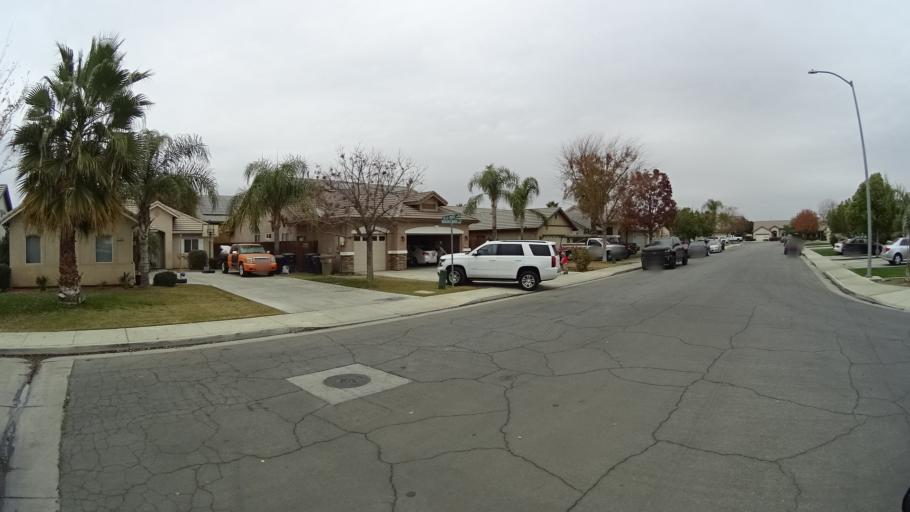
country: US
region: California
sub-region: Kern County
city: Greenfield
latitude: 35.2877
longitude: -119.0368
